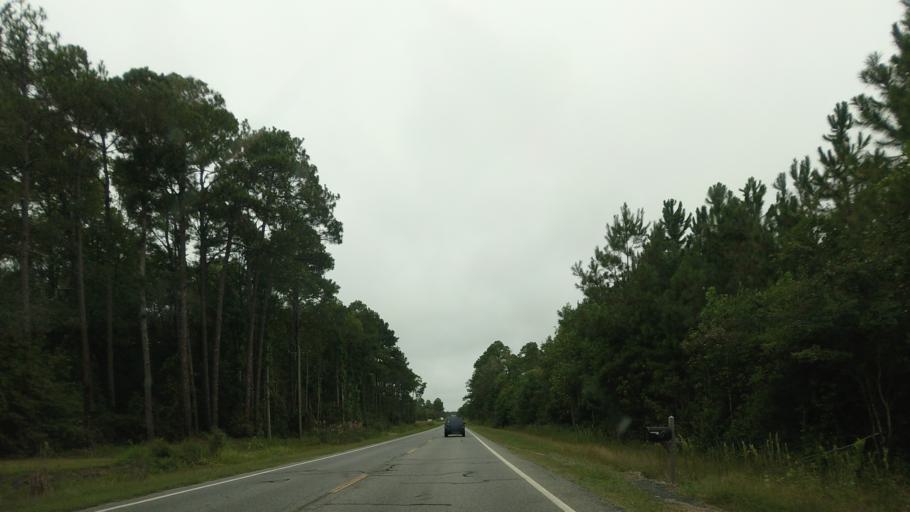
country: US
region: Georgia
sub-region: Irwin County
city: Ocilla
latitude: 31.5623
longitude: -83.2529
